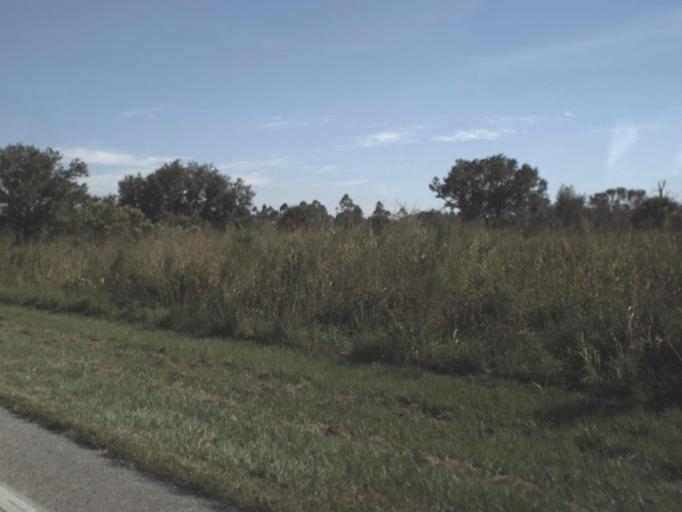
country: US
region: Florida
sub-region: Glades County
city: Moore Haven
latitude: 26.9109
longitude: -81.2755
